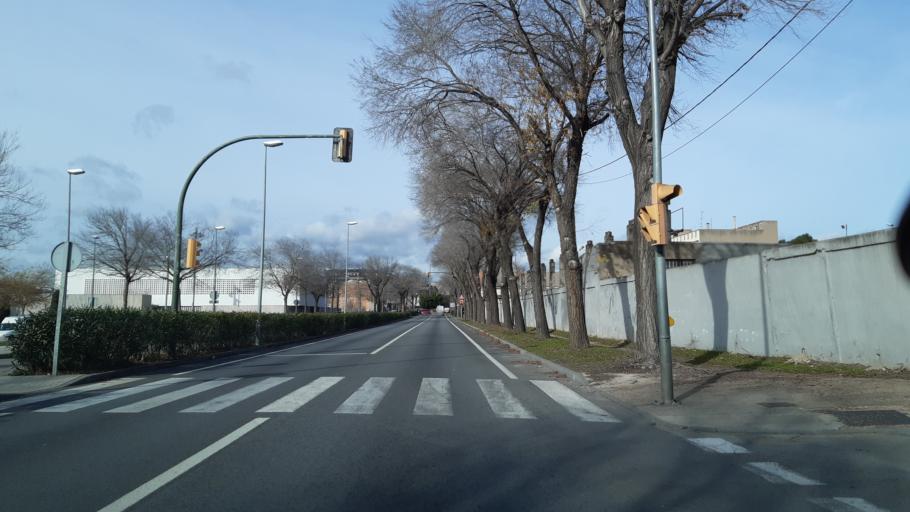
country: ES
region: Catalonia
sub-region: Provincia de Barcelona
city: Vilanova del Cami
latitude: 41.5734
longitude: 1.6434
